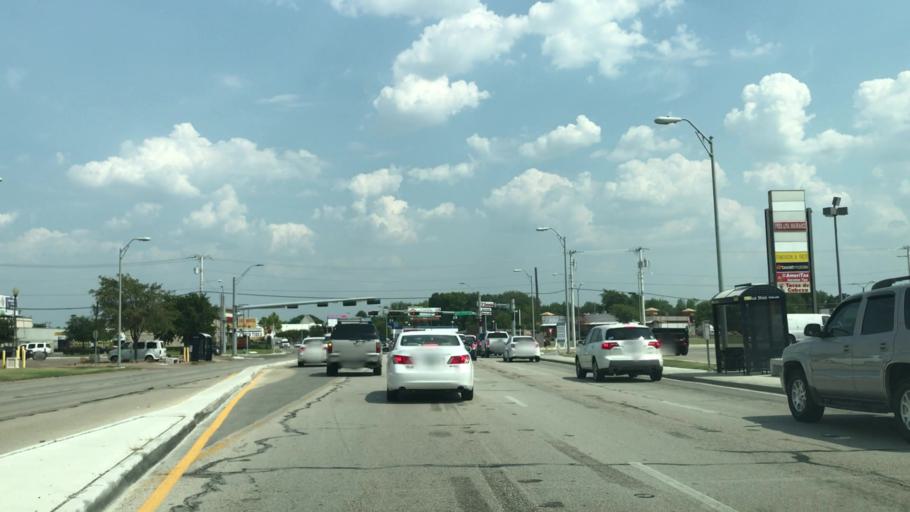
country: US
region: Texas
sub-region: Dallas County
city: University Park
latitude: 32.8570
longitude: -96.8725
